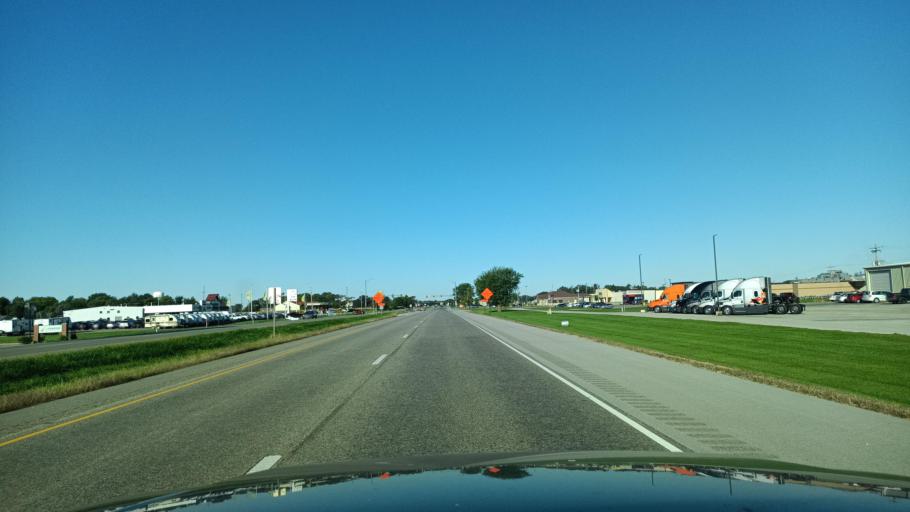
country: US
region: Illinois
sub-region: Warren County
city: Monmouth
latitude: 40.9249
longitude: -90.6370
